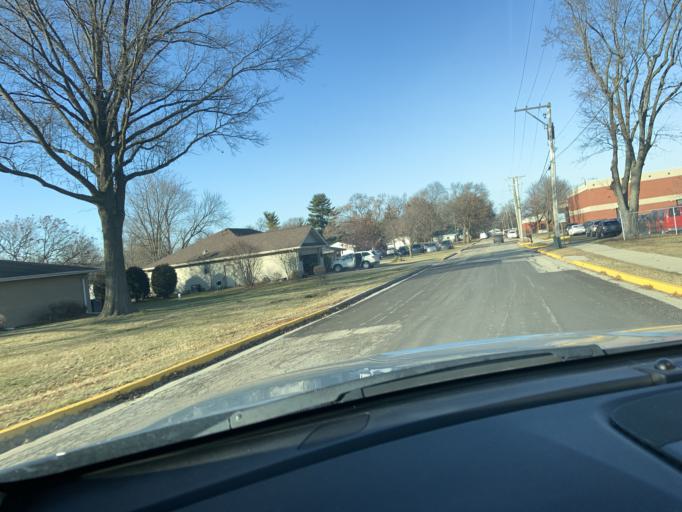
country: US
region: Illinois
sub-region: LaSalle County
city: Seneca
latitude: 41.3070
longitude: -88.6079
